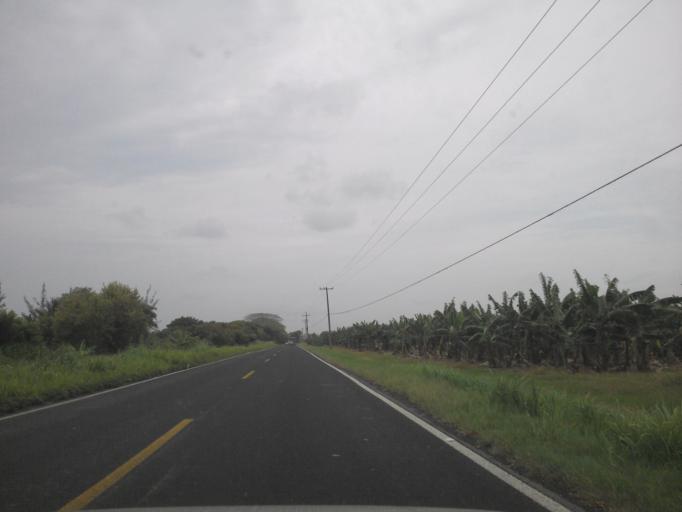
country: MX
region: Veracruz
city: Nautla
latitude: 20.2232
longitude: -96.7868
